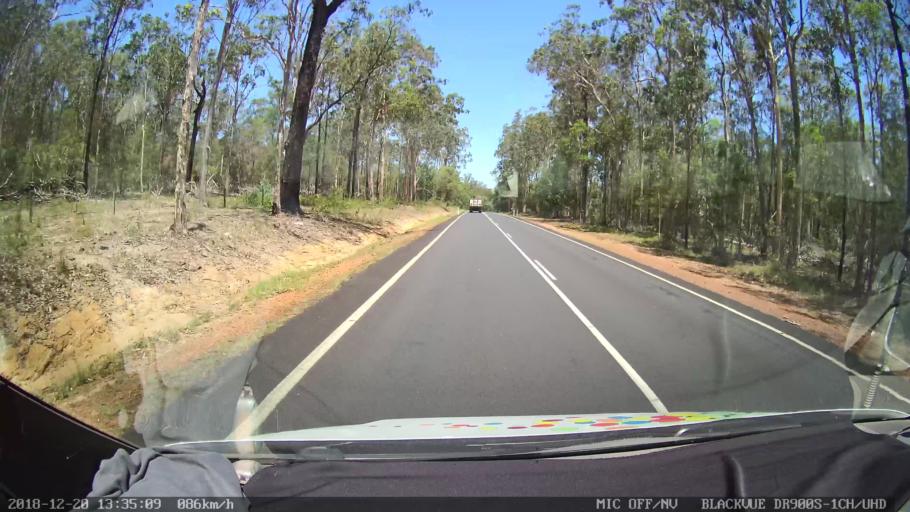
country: AU
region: New South Wales
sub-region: Clarence Valley
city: Gordon
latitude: -29.2666
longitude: 152.9887
